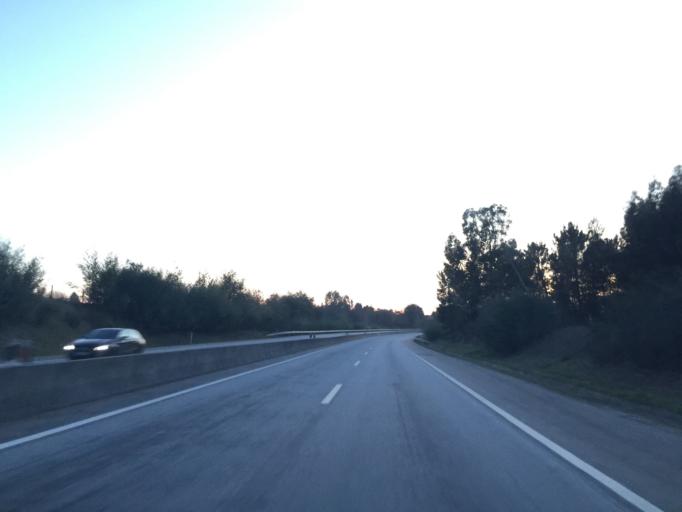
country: PT
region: Viseu
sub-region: Santa Comba Dao
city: Santa Comba Dao
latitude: 40.4027
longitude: -8.0781
